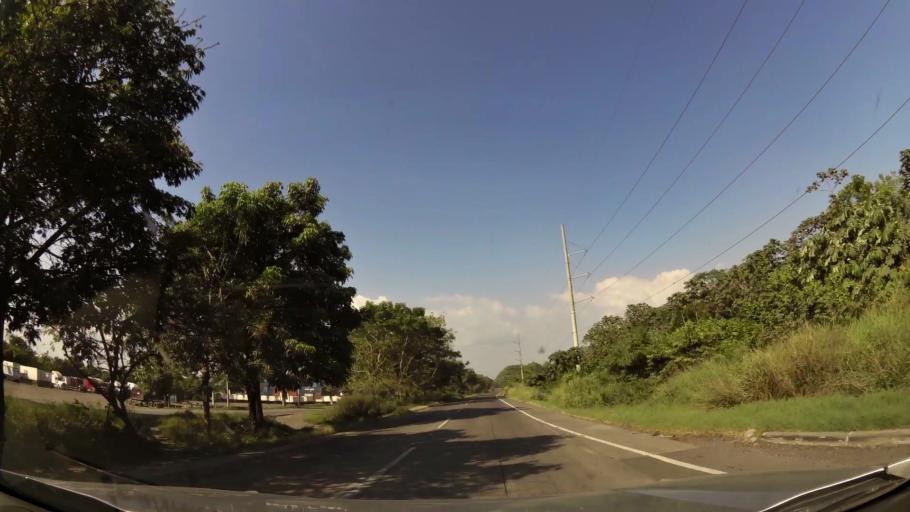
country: GT
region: Escuintla
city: Puerto San Jose
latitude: 13.9660
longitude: -90.7885
